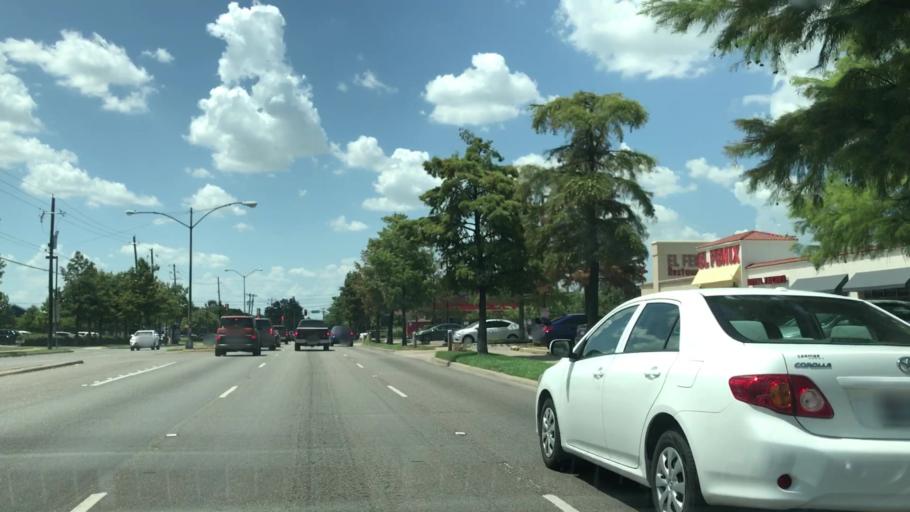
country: US
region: Texas
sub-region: Dallas County
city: University Park
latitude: 32.8288
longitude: -96.8251
